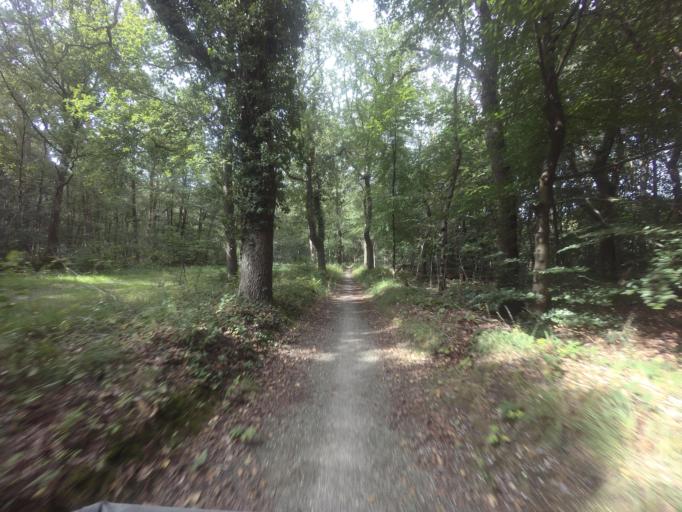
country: NL
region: Drenthe
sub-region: Gemeente Assen
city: Assen
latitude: 53.0451
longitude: 6.4462
